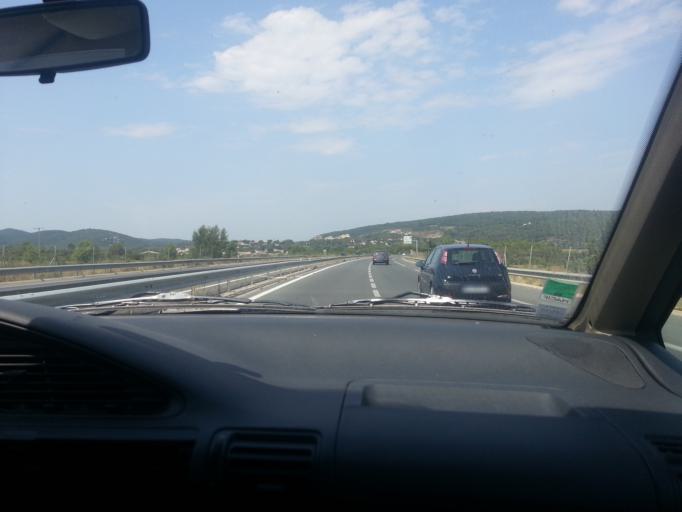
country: FR
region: Languedoc-Roussillon
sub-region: Departement de l'Herault
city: Montarnaud
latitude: 43.6282
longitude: 3.7019
